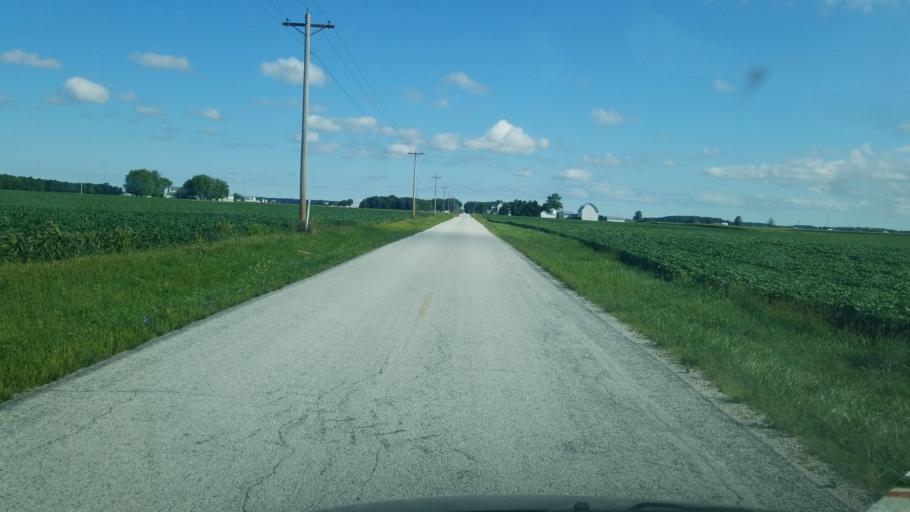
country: US
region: Ohio
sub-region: Wyandot County
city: Carey
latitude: 41.0331
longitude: -83.3630
